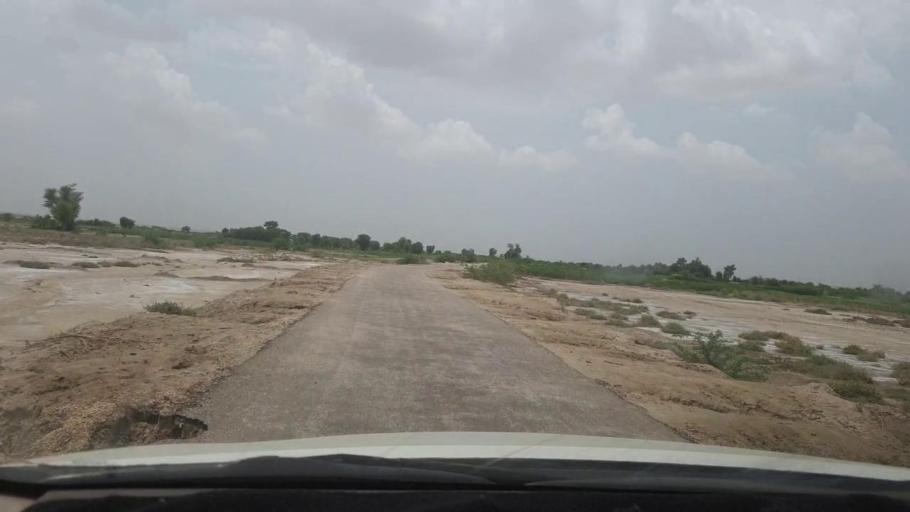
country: PK
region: Sindh
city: Khairpur
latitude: 27.3927
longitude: 68.9913
